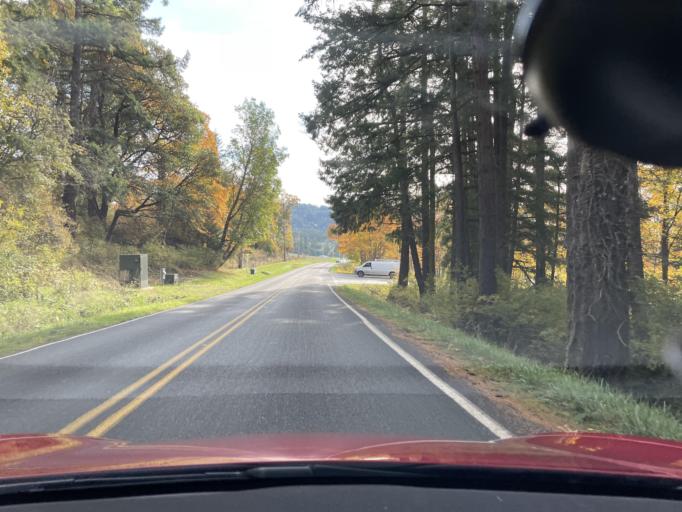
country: US
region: Washington
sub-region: San Juan County
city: Friday Harbor
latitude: 48.5791
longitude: -123.1430
